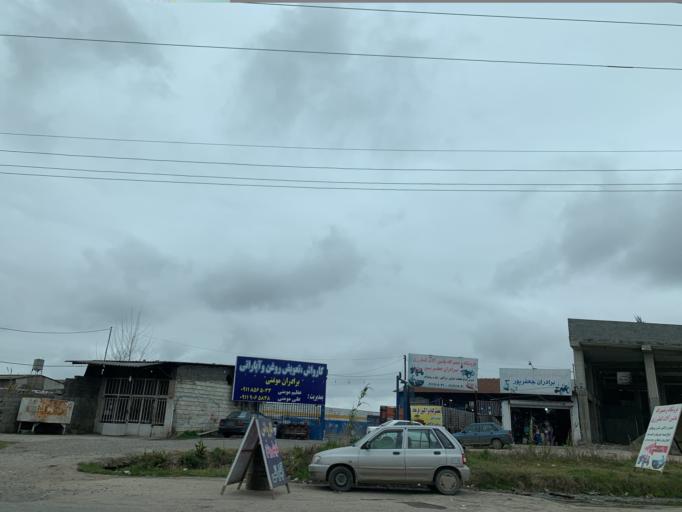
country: IR
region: Mazandaran
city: Babol
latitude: 36.5172
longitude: 52.5786
